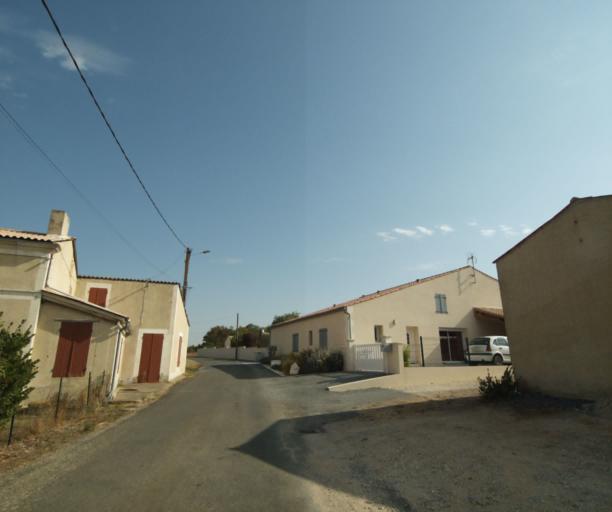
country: FR
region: Poitou-Charentes
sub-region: Departement de la Charente-Maritime
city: Tonnay-Charente
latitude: 45.9649
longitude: -0.8768
